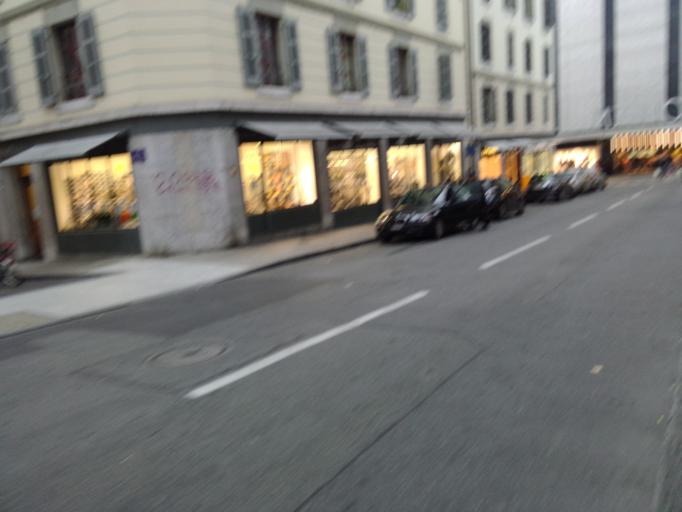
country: CH
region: Geneva
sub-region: Geneva
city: Geneve
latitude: 46.2080
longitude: 6.1436
